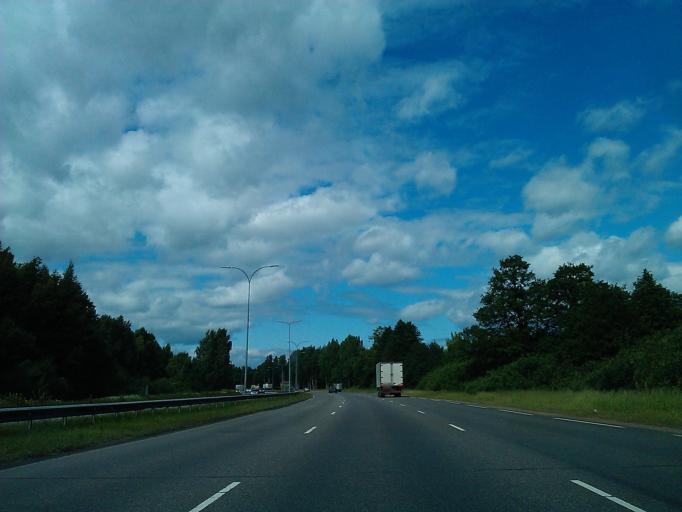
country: LV
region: Babite
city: Pinki
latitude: 56.9492
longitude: 23.9864
